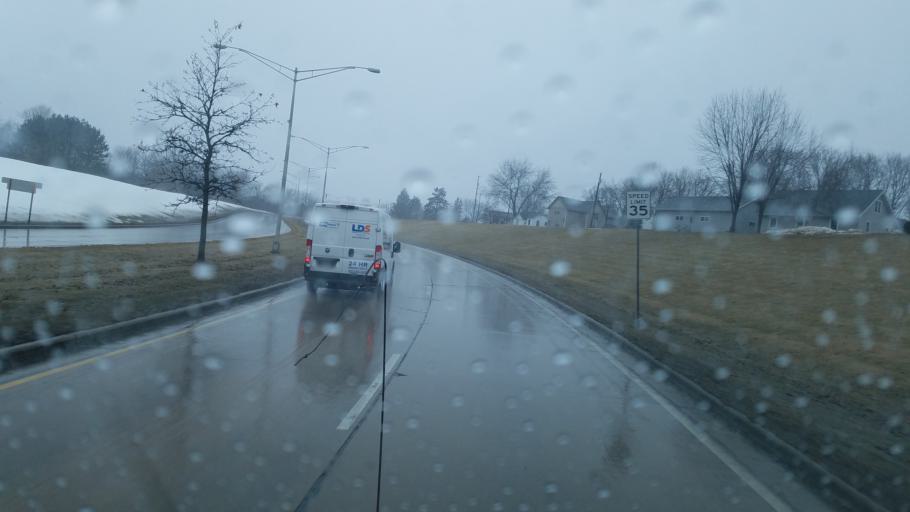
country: US
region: Wisconsin
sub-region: Wood County
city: Marshfield
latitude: 44.6714
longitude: -90.1826
